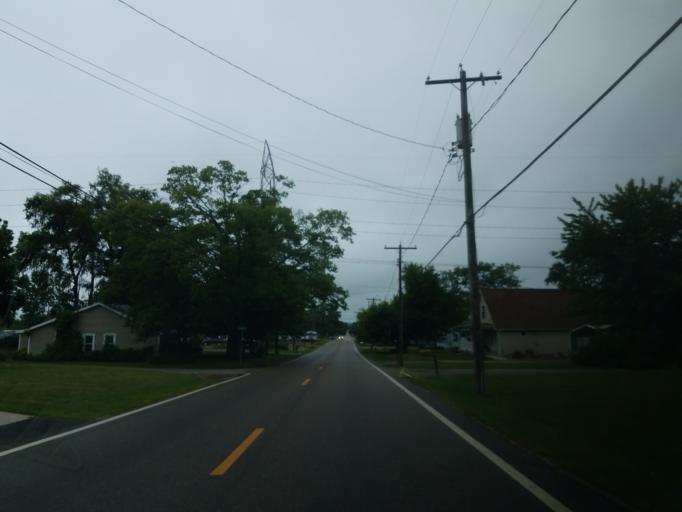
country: US
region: Illinois
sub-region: McLean County
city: Bloomington
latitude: 40.4614
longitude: -88.9816
